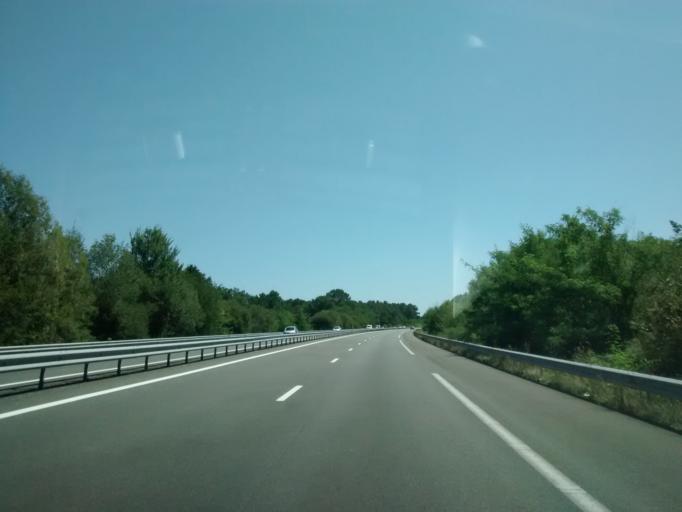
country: FR
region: Aquitaine
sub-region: Departement de la Gironde
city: Saint-Medard-de-Guizieres
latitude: 45.0061
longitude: -0.0287
